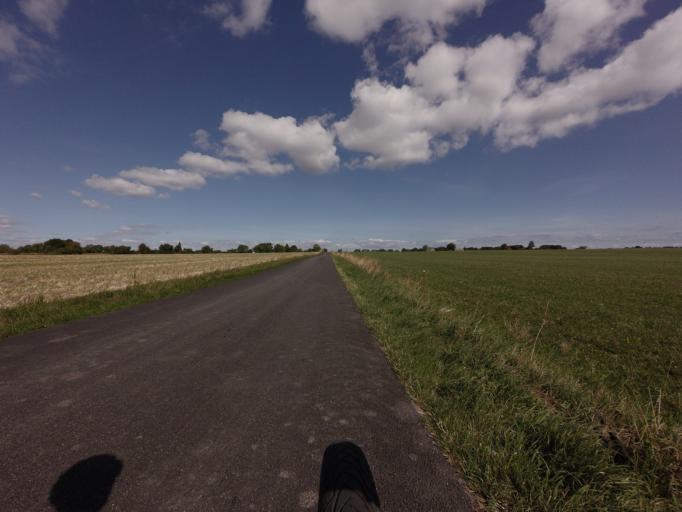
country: DK
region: Zealand
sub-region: Vordingborg Kommune
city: Stege
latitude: 54.9702
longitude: 12.3590
